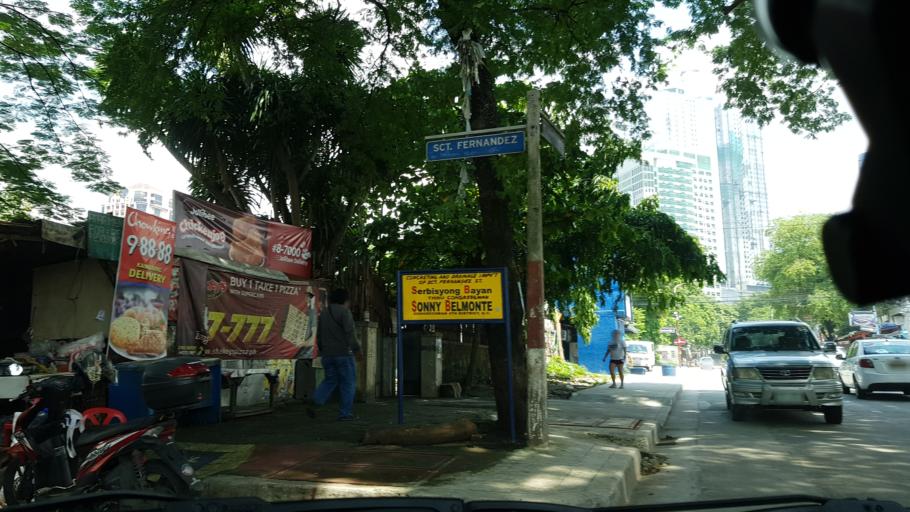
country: PH
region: Metro Manila
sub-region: Quezon City
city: Quezon City
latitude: 14.6313
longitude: 121.0411
